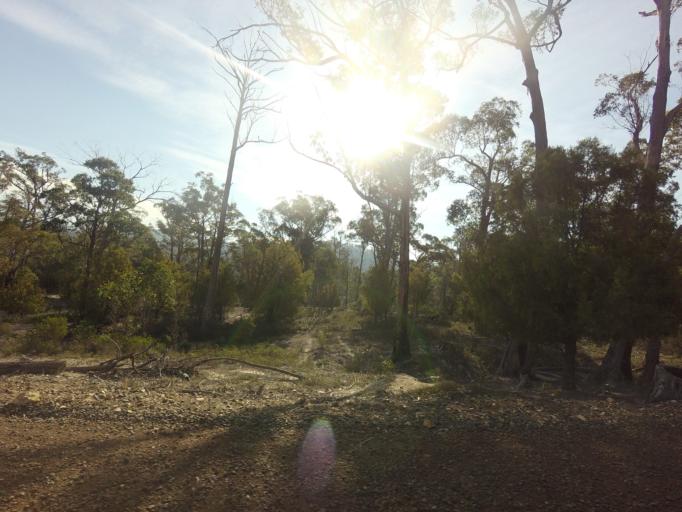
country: AU
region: Tasmania
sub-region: Sorell
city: Sorell
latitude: -42.5288
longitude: 147.4547
